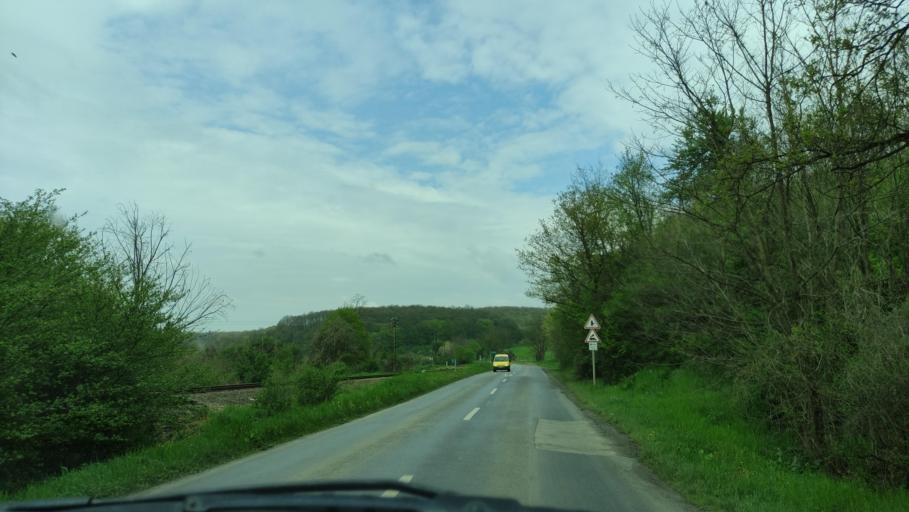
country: HU
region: Baranya
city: Komlo
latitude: 46.2244
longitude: 18.2375
